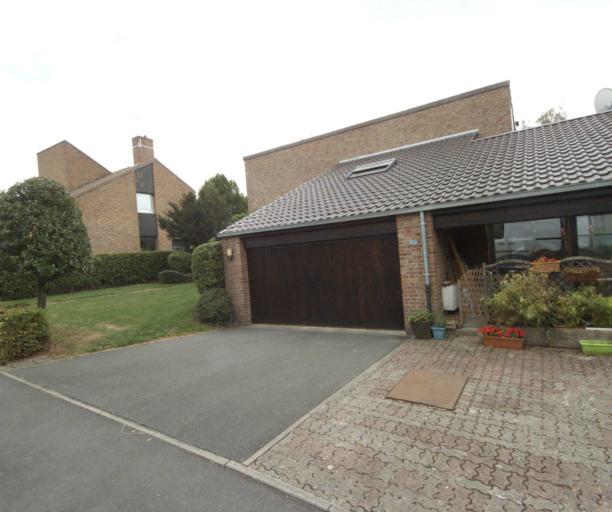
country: FR
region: Nord-Pas-de-Calais
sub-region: Departement du Nord
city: Gruson
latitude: 50.5985
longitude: 3.2044
